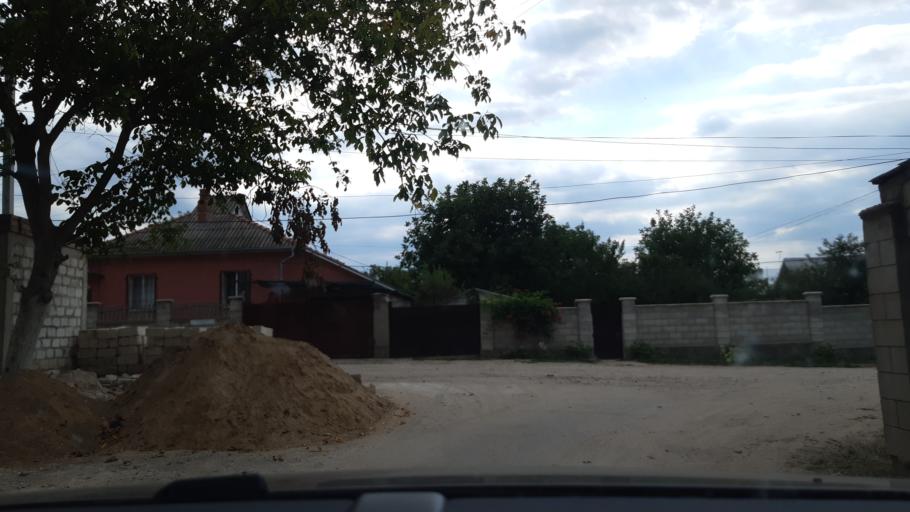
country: MD
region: Chisinau
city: Vatra
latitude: 47.0583
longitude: 28.7330
